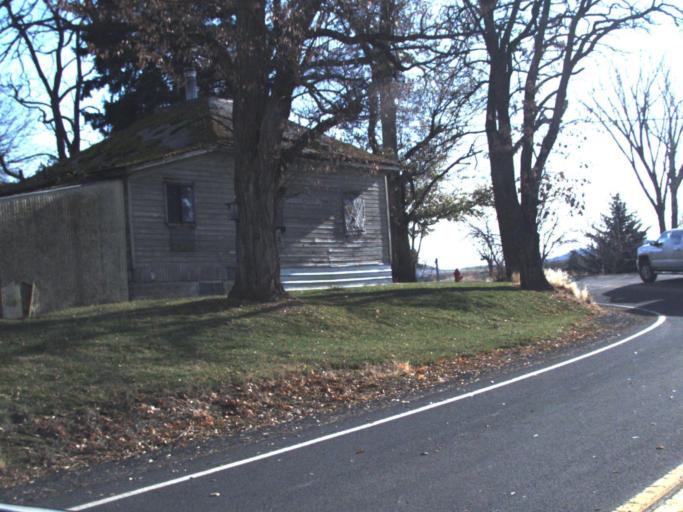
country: US
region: Idaho
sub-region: Latah County
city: Moscow
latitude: 46.9117
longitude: -117.0875
